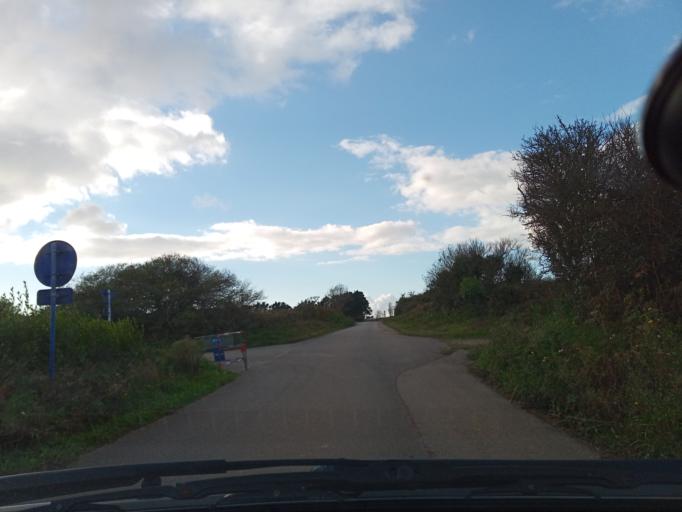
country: FR
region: Brittany
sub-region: Departement du Finistere
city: Plouhinec
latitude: 48.0174
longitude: -4.4957
